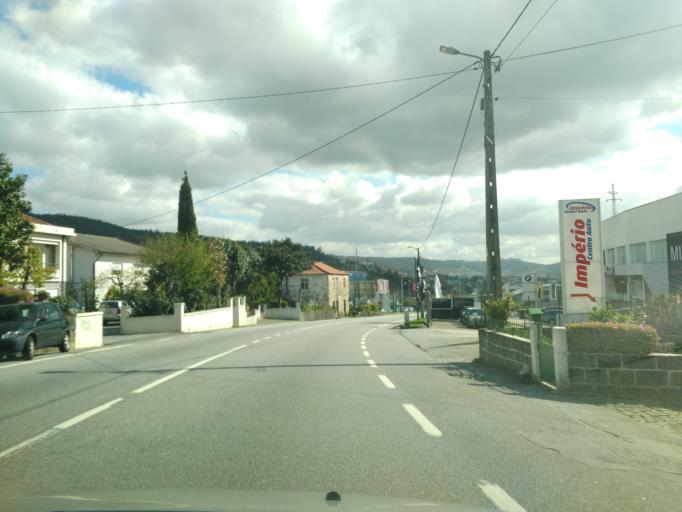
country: PT
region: Braga
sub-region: Braga
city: Braga
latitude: 41.5283
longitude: -8.4179
